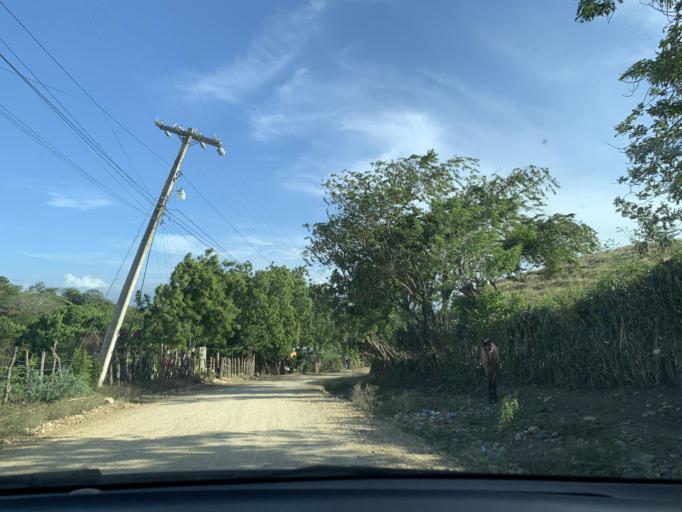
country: DO
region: Puerto Plata
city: Luperon
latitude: 19.8715
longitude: -70.9403
